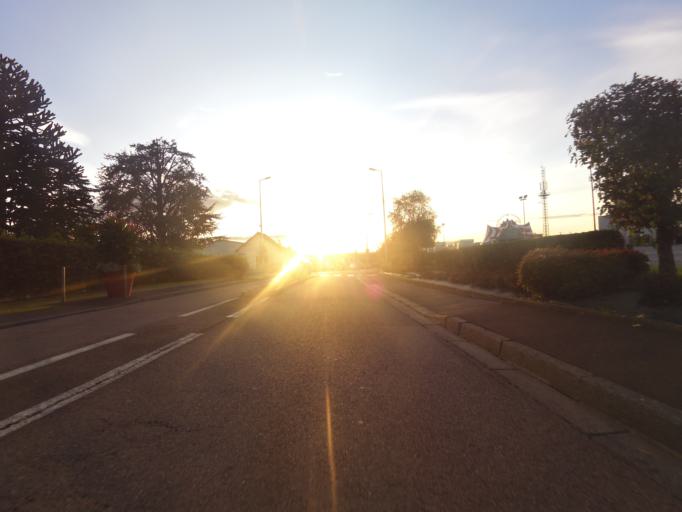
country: FR
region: Lower Normandy
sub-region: Departement du Calvados
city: La Vespiere
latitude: 49.0242
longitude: 0.4165
